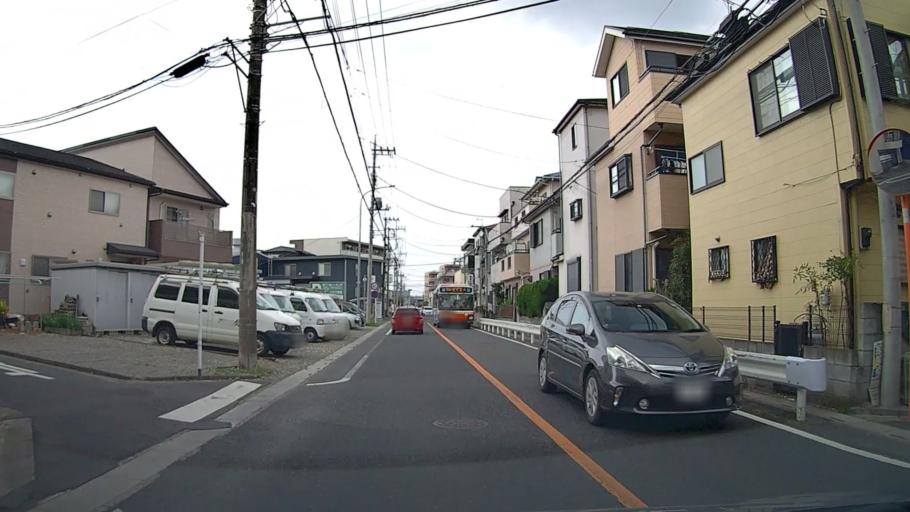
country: JP
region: Saitama
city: Asaka
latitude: 35.8058
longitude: 139.5997
